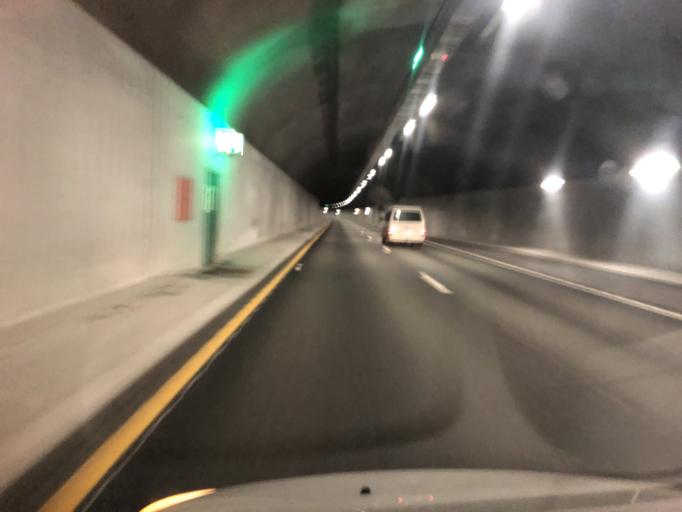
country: NO
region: Aust-Agder
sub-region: Tvedestrand
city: Tvedestrand
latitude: 58.6316
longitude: 8.8990
